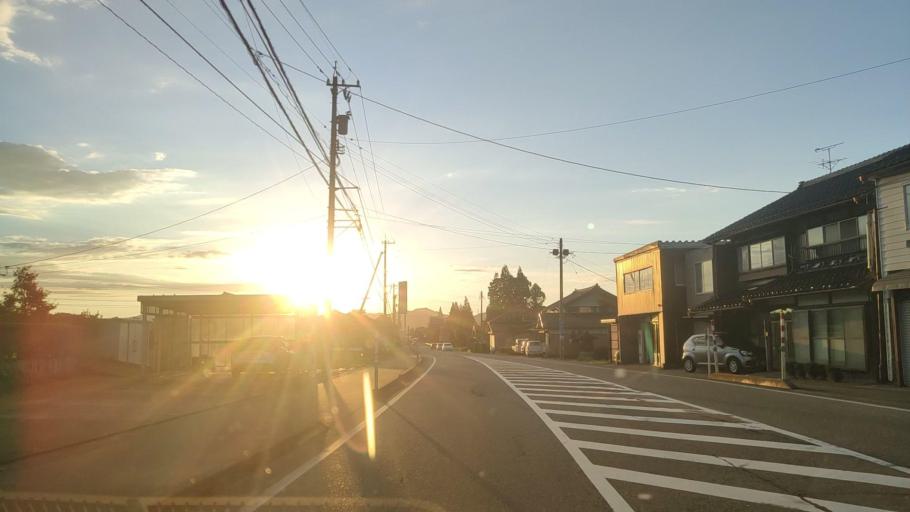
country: JP
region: Toyama
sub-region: Oyabe Shi
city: Oyabe
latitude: 36.6313
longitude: 136.8704
